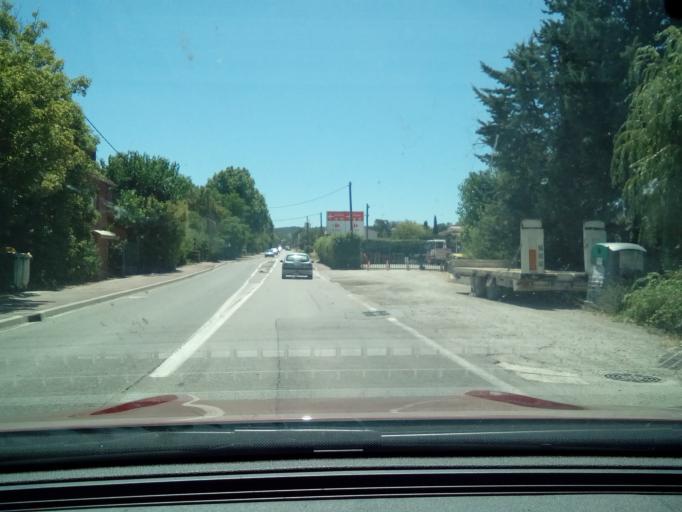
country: FR
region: Provence-Alpes-Cote d'Azur
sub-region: Departement des Bouches-du-Rhone
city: Chateauneuf-le-Rouge
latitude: 43.4817
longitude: 5.5337
